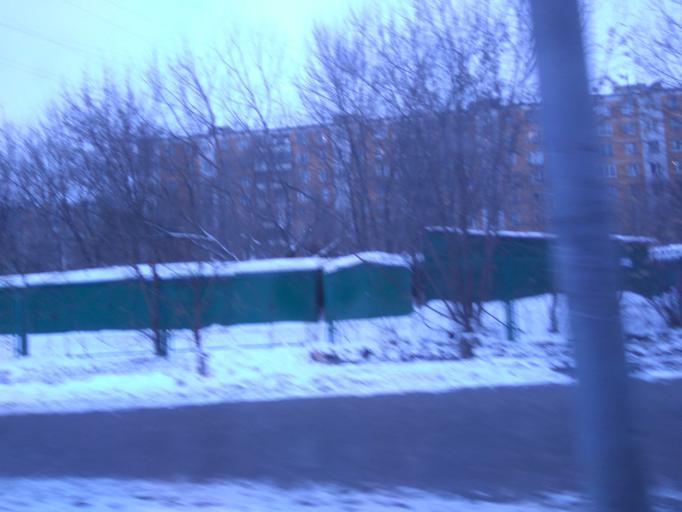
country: RU
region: Moscow
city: Gol'yanovo
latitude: 55.8144
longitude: 37.8281
